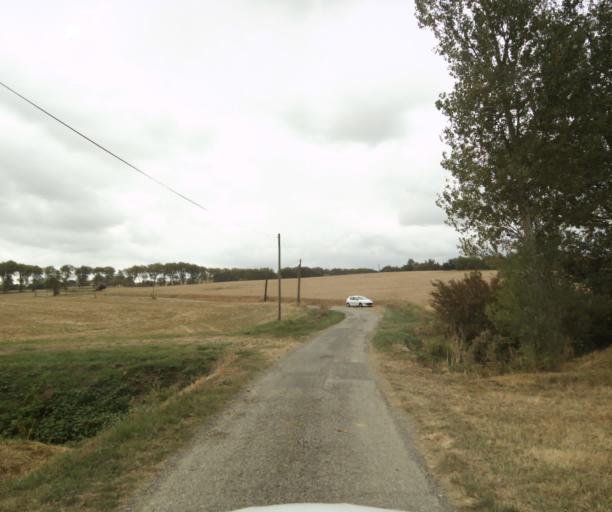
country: FR
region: Midi-Pyrenees
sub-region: Departement de la Haute-Garonne
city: Villefranche-de-Lauragais
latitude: 43.4169
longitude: 1.7367
